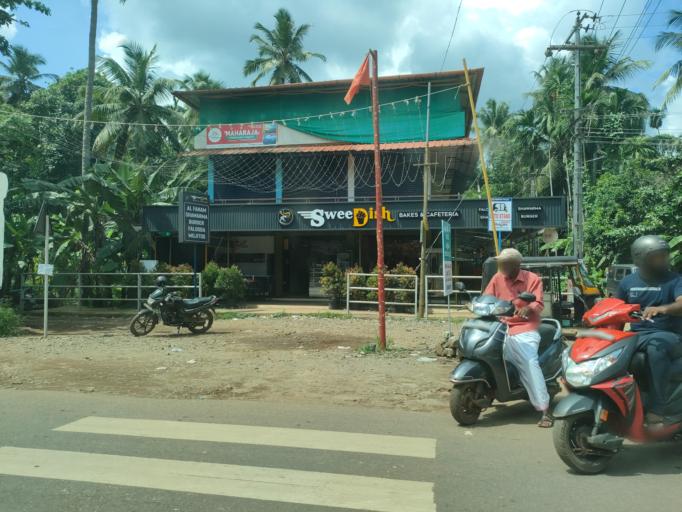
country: IN
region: Kerala
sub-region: Kozhikode
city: Kunnamangalam
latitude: 11.2693
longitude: 75.8587
